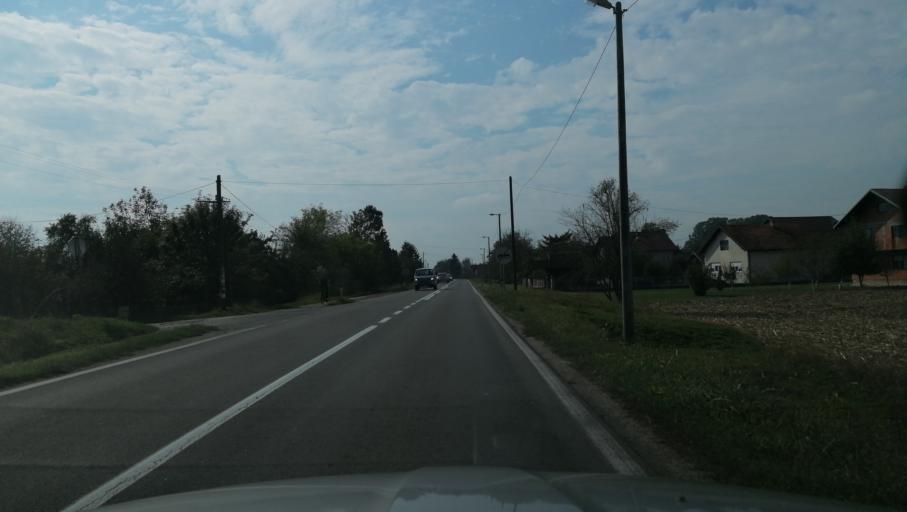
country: BA
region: Republika Srpska
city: Balatun
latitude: 44.8576
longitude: 19.3224
